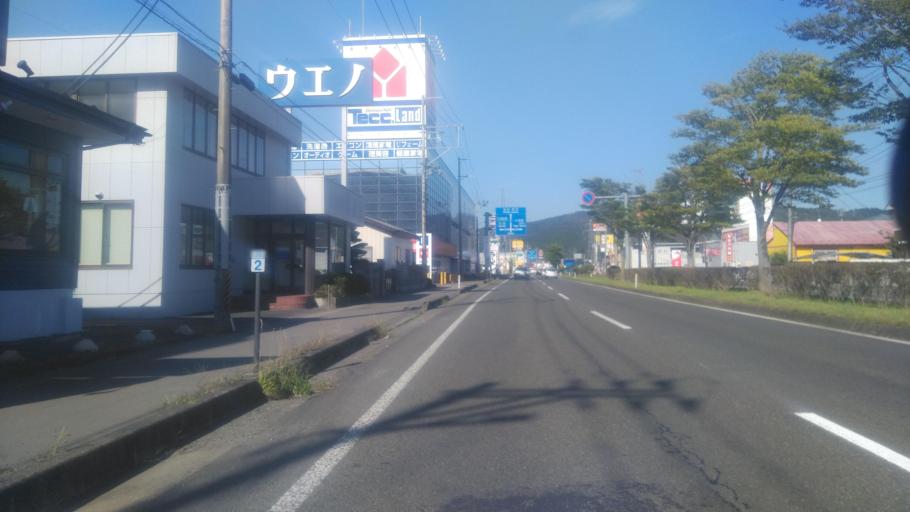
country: JP
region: Miyagi
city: Okawara
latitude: 38.0583
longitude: 140.7353
